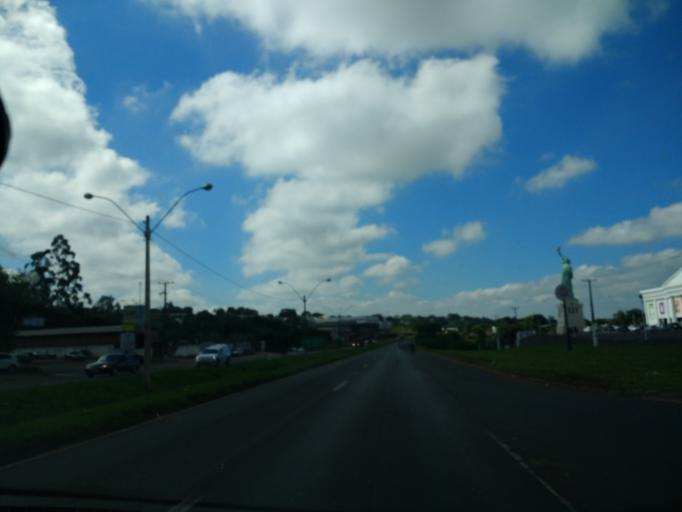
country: BR
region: Parana
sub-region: Umuarama
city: Umuarama
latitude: -23.7796
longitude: -53.3025
